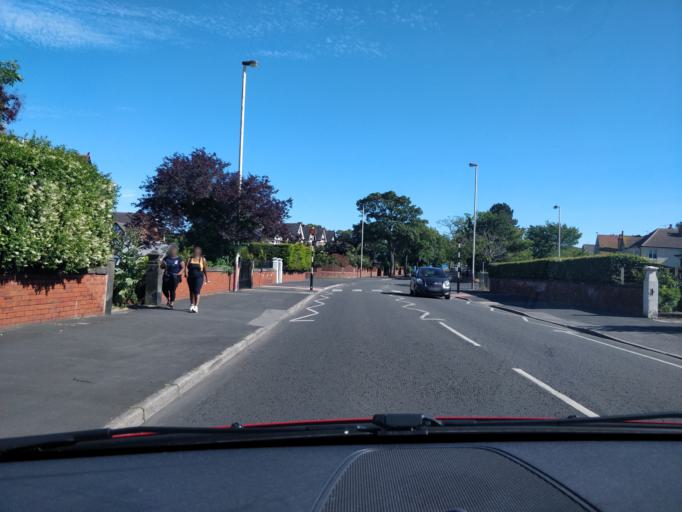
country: GB
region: England
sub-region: Sefton
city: Southport
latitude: 53.6490
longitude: -2.9770
